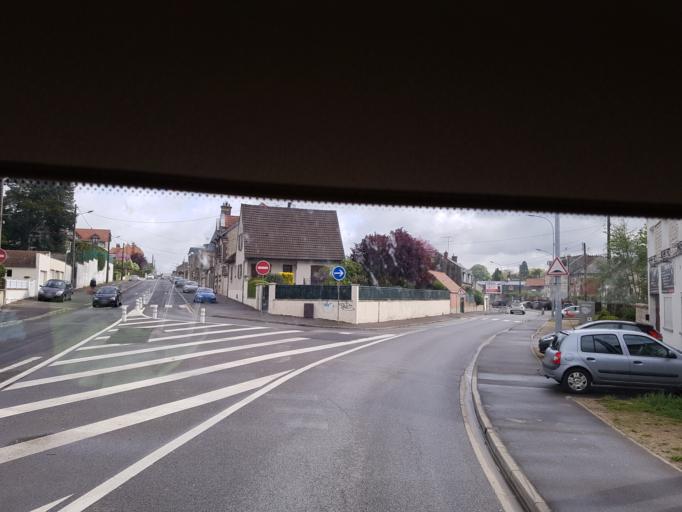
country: FR
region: Picardie
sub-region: Departement de l'Aisne
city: Soissons
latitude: 49.3729
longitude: 3.3250
